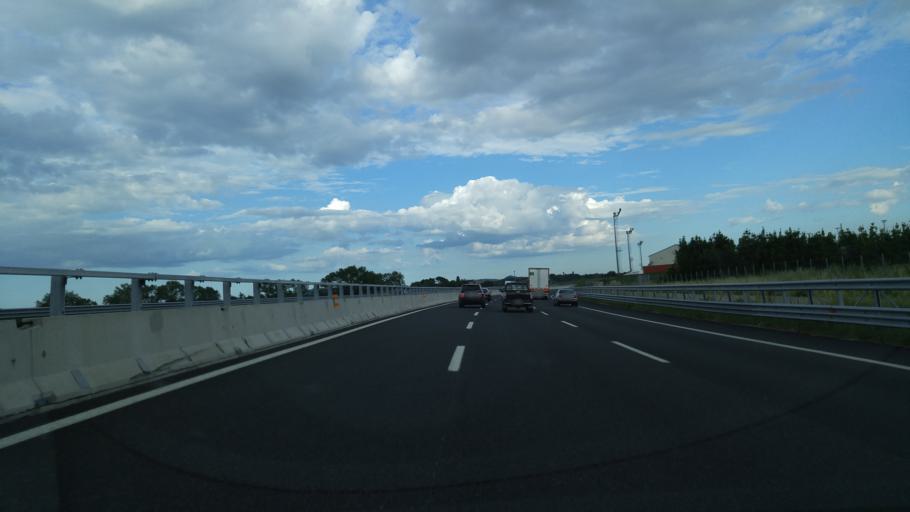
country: IT
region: Emilia-Romagna
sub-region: Provincia di Rimini
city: Santa Monica-Cella
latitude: 43.9676
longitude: 12.6838
